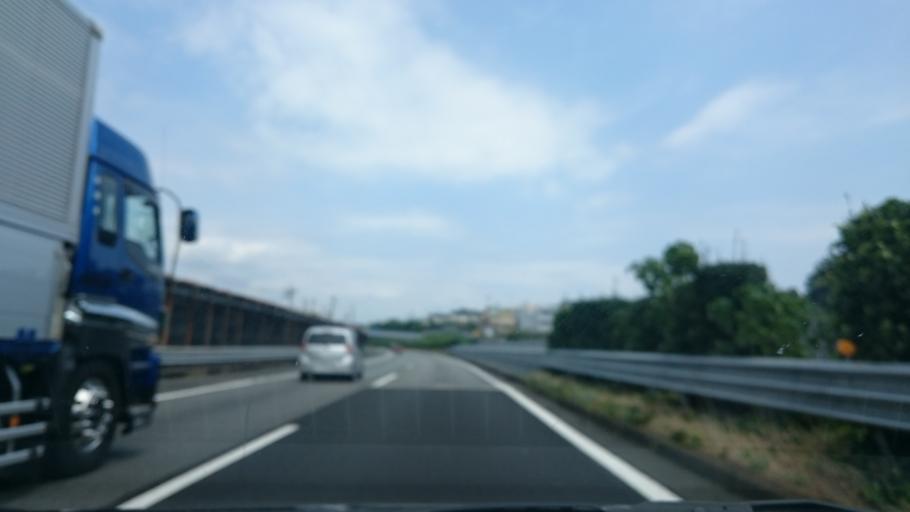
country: JP
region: Shizuoka
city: Shizuoka-shi
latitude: 34.9678
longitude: 138.4290
